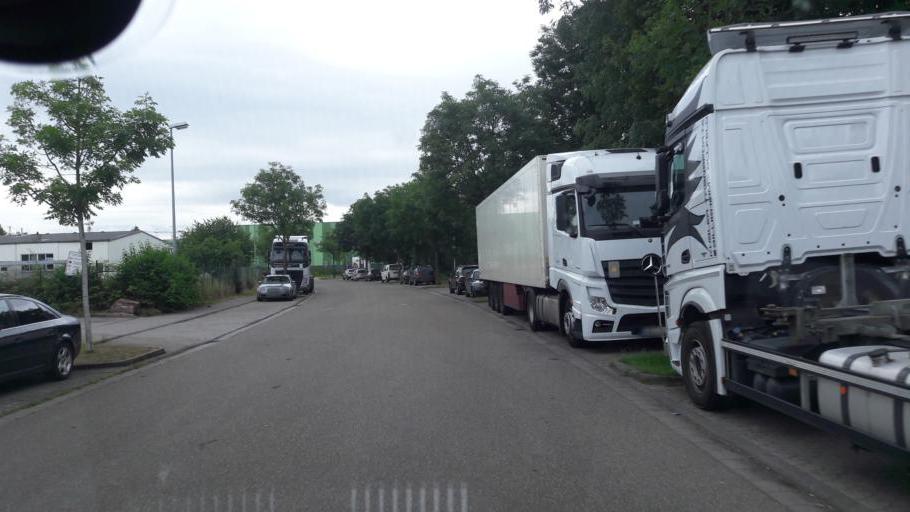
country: DE
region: Baden-Wuerttemberg
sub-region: Karlsruhe Region
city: Bruchsal
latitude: 49.1267
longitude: 8.5673
